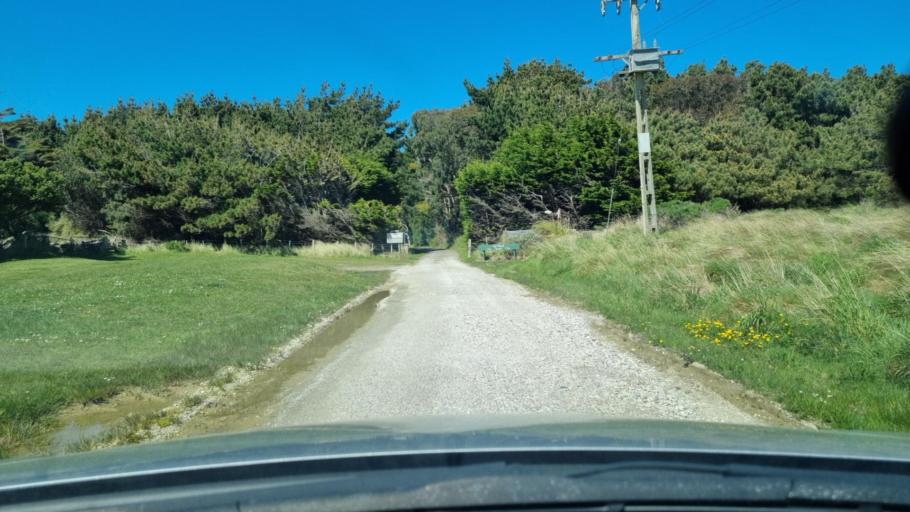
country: NZ
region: Southland
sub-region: Invercargill City
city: Invercargill
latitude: -46.4405
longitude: 168.2399
